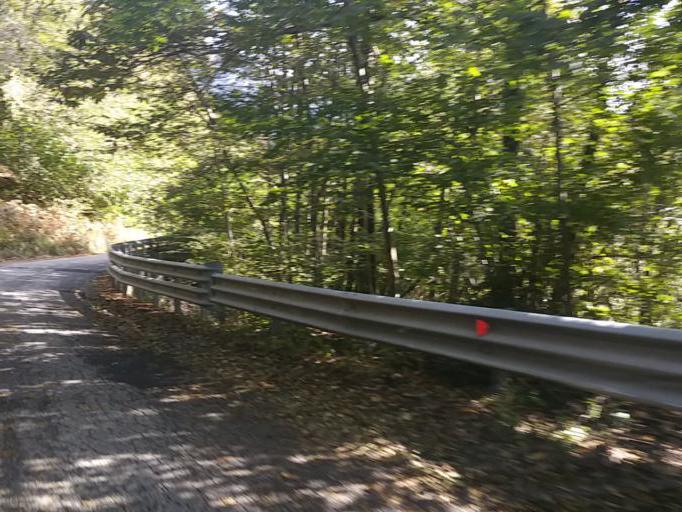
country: IT
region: Piedmont
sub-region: Provincia Verbano-Cusio-Ossola
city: Cursolo
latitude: 46.0946
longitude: 8.5647
